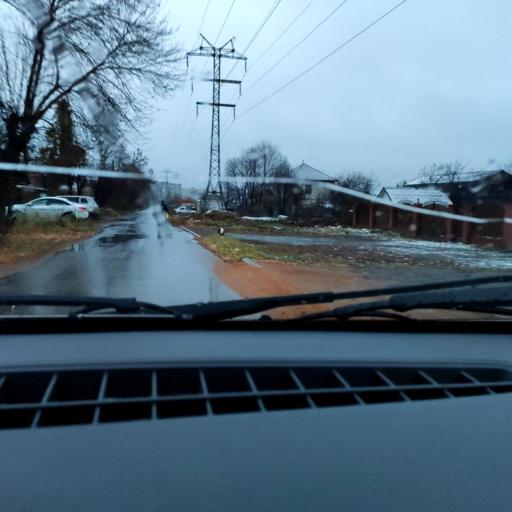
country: RU
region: Bashkortostan
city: Avdon
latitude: 54.6895
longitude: 55.8102
